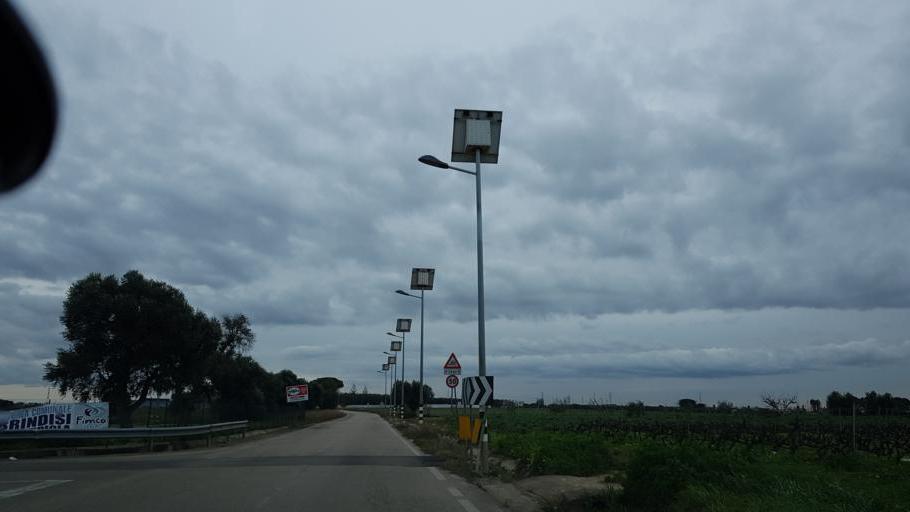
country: IT
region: Apulia
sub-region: Provincia di Brindisi
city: La Rosa
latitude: 40.6143
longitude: 17.9448
